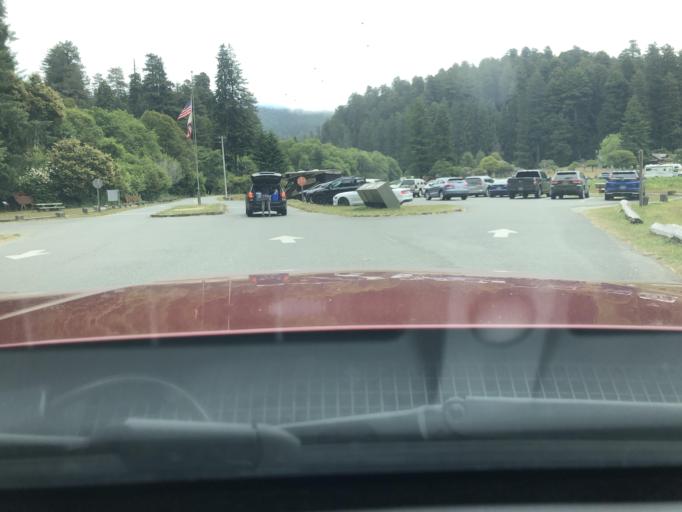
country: US
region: California
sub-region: Humboldt County
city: Westhaven-Moonstone
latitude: 41.3636
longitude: -124.0233
